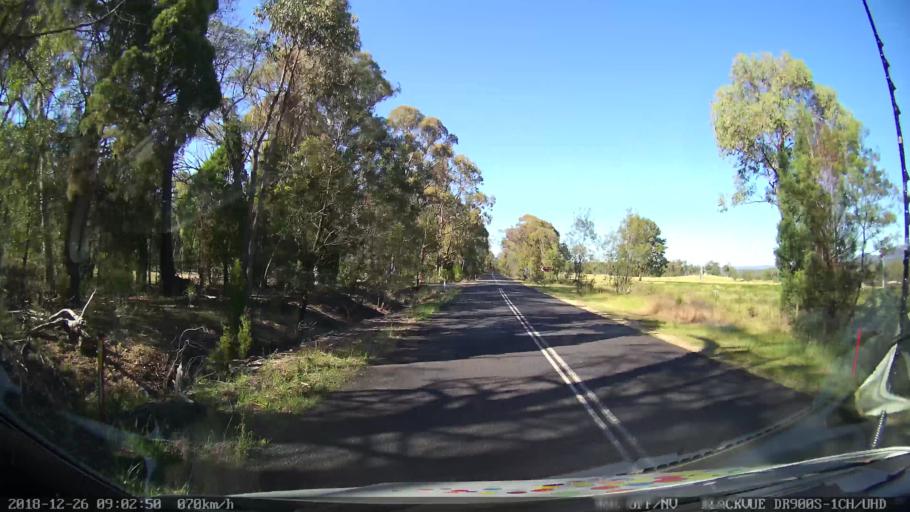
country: AU
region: New South Wales
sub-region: Mid-Western Regional
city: Kandos
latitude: -32.6568
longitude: 150.0171
